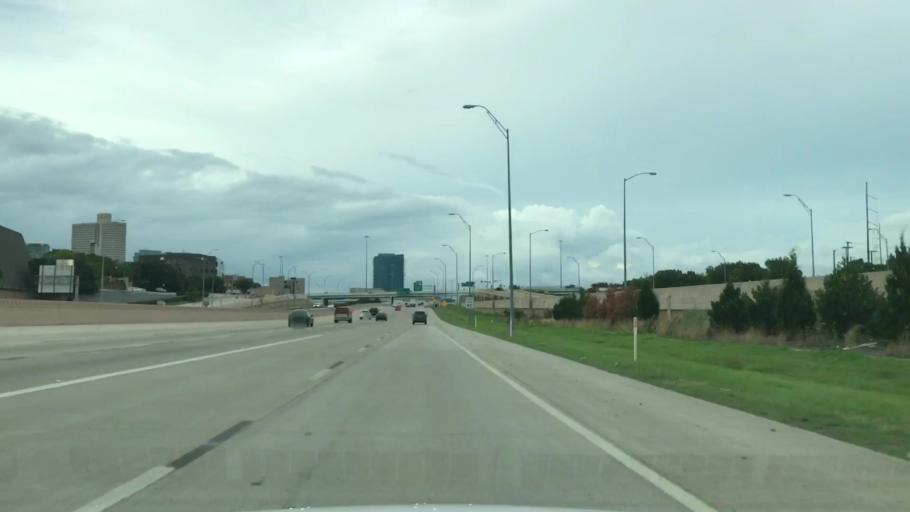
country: US
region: Texas
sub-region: Tarrant County
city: Fort Worth
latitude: 32.7402
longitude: -97.3465
